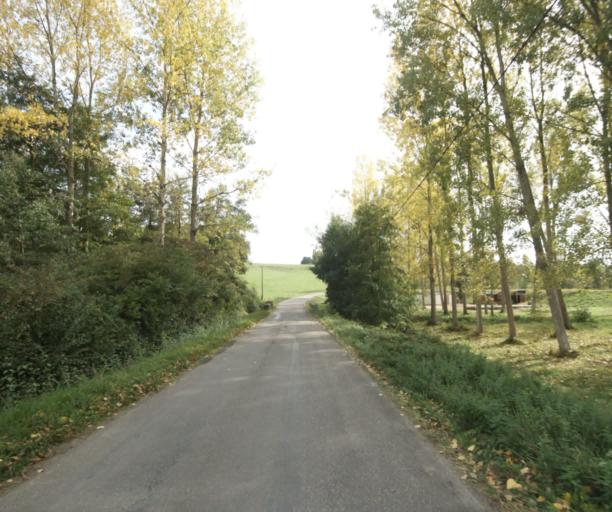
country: FR
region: Midi-Pyrenees
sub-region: Departement du Gers
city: Eauze
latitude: 43.8426
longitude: 0.1110
